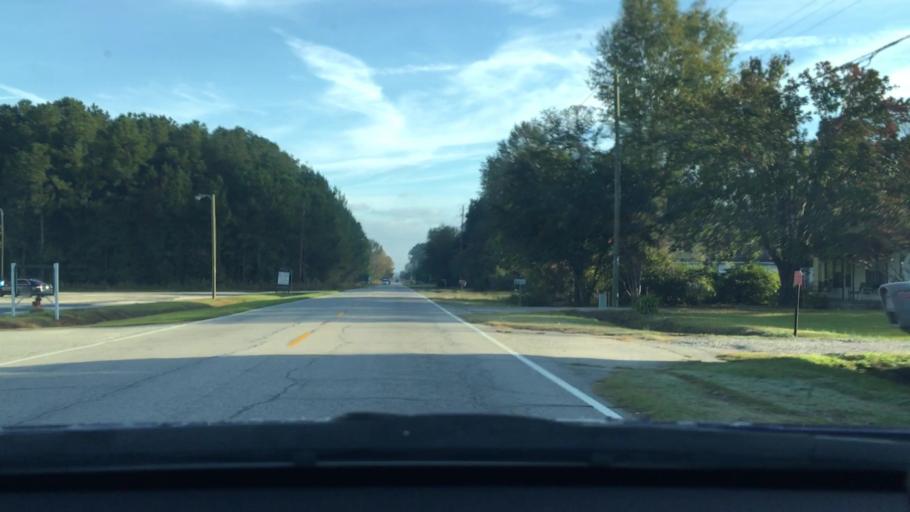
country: US
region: South Carolina
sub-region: Sumter County
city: East Sumter
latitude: 33.9412
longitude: -80.3167
